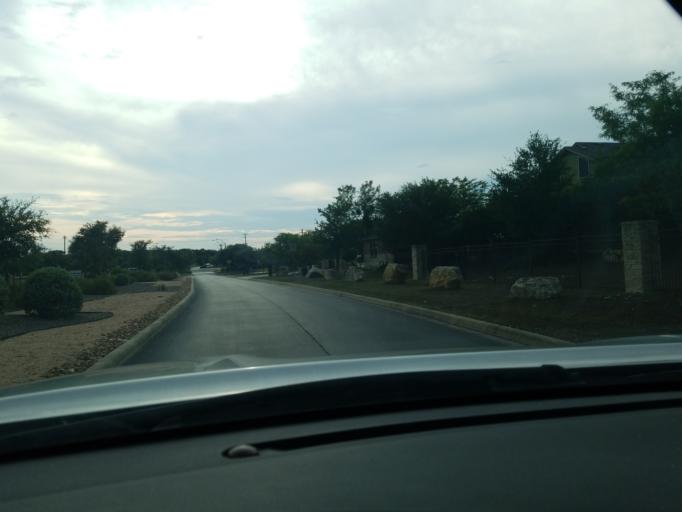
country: US
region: Texas
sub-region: Comal County
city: Bulverde
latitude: 29.8498
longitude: -98.4062
